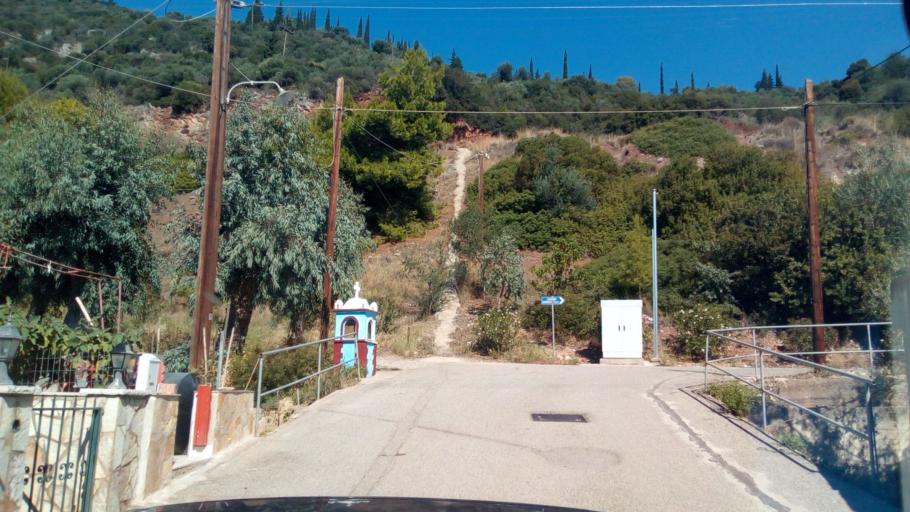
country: GR
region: West Greece
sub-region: Nomos Achaias
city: Kamarai
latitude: 38.3947
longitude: 22.0525
